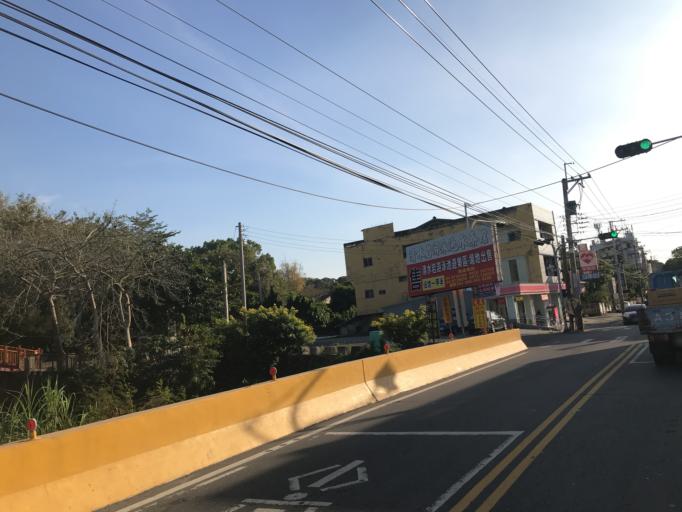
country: TW
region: Taiwan
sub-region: Nantou
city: Nantou
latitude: 23.8892
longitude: 120.6095
